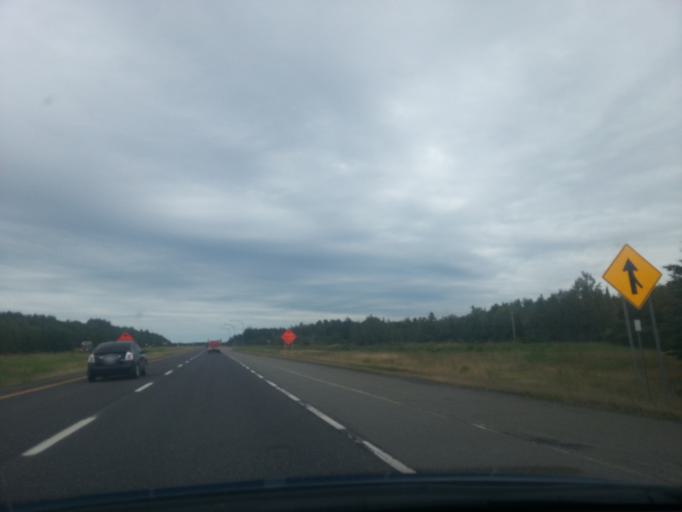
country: CA
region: Quebec
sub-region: Bas-Saint-Laurent
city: Riviere-du-Loup
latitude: 47.6352
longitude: -69.7138
